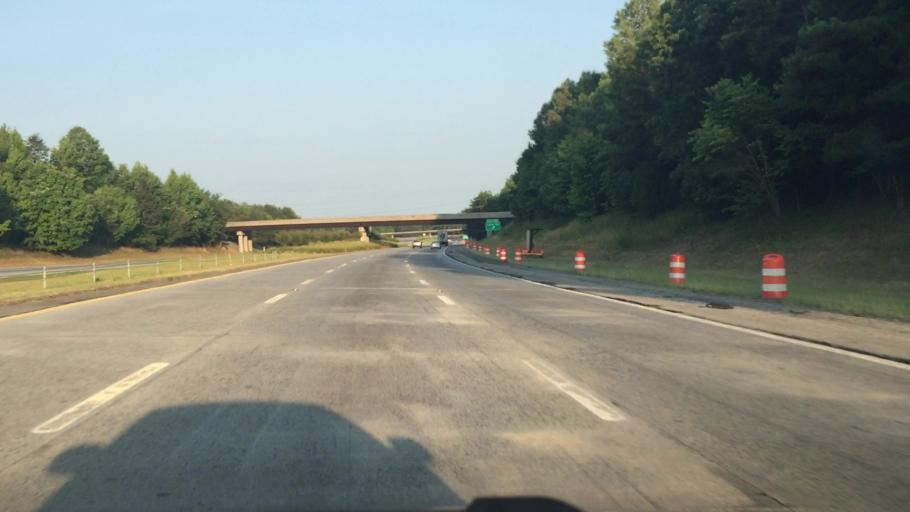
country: US
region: North Carolina
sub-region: Davidson County
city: Thomasville
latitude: 35.8551
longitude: -80.0940
